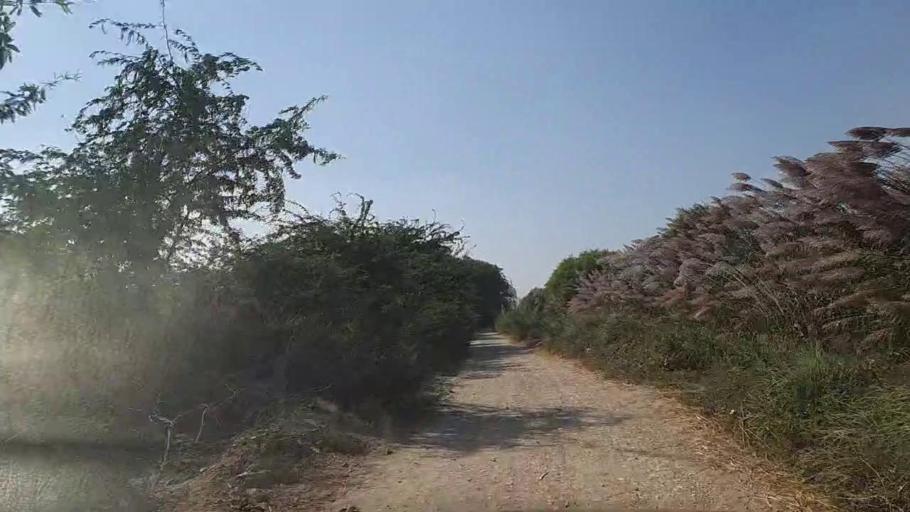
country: PK
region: Sindh
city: Daro Mehar
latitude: 24.8377
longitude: 68.1128
